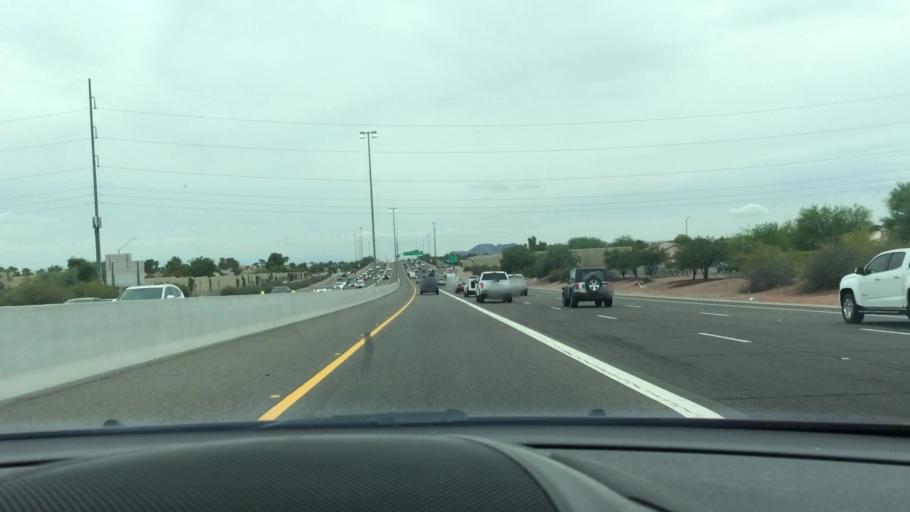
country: US
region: Arizona
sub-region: Maricopa County
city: Paradise Valley
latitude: 33.6678
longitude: -112.0552
